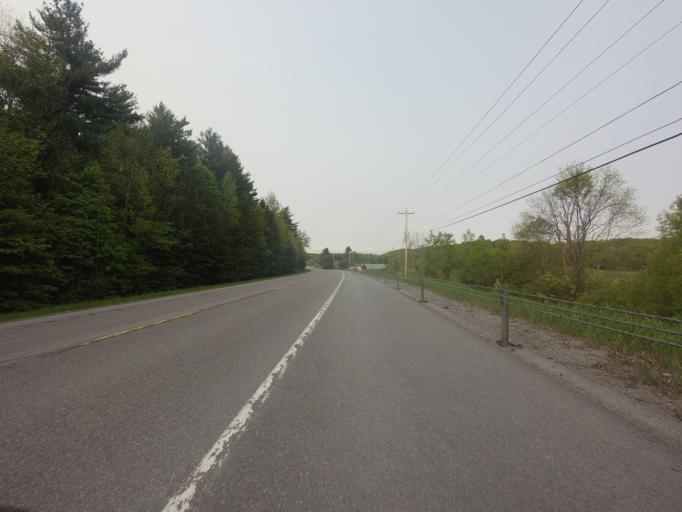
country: US
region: New York
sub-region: Jefferson County
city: Carthage
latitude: 44.1031
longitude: -75.4117
